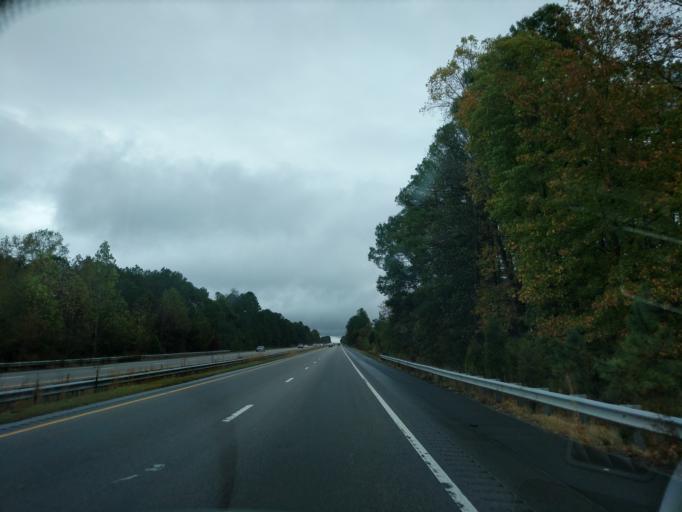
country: US
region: North Carolina
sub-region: Durham County
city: Gorman
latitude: 36.0402
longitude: -78.8245
